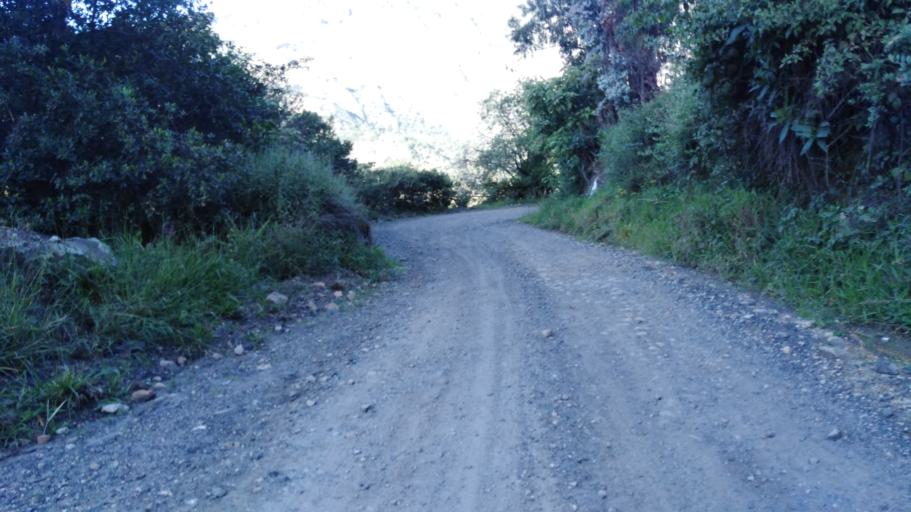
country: CO
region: Boyaca
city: San Mateo
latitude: 6.4023
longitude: -72.5644
